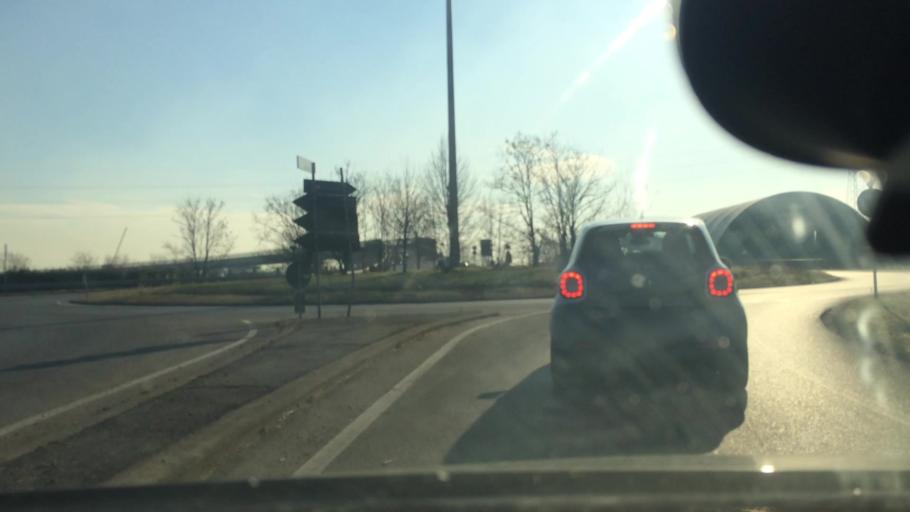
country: IT
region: Lombardy
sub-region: Citta metropolitana di Milano
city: Arluno
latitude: 45.5024
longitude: 8.9295
